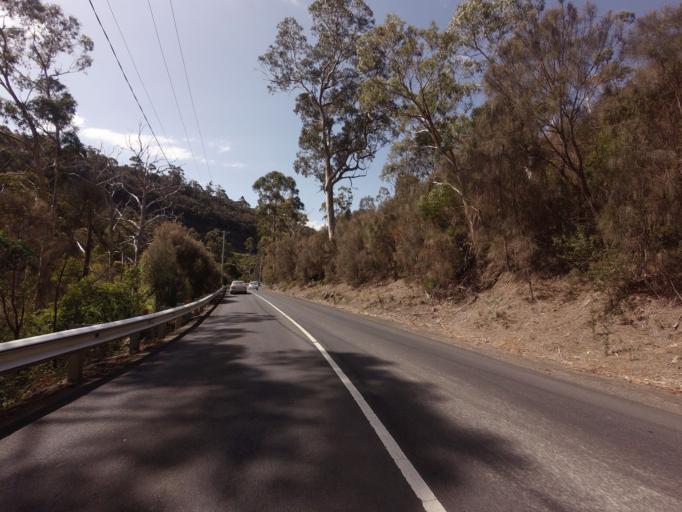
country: AU
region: Tasmania
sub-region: Hobart
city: Dynnyrne
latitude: -42.9084
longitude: 147.3125
